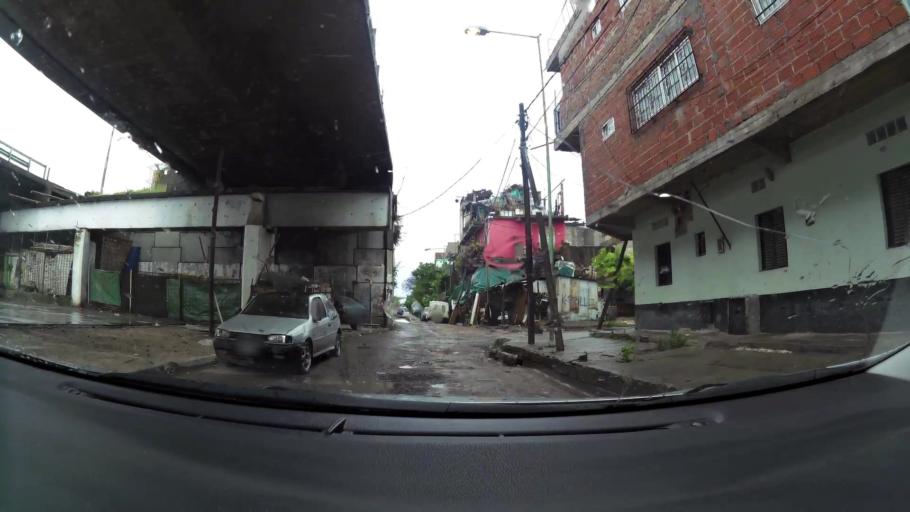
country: AR
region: Buenos Aires F.D.
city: Villa Lugano
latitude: -34.6561
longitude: -58.4591
